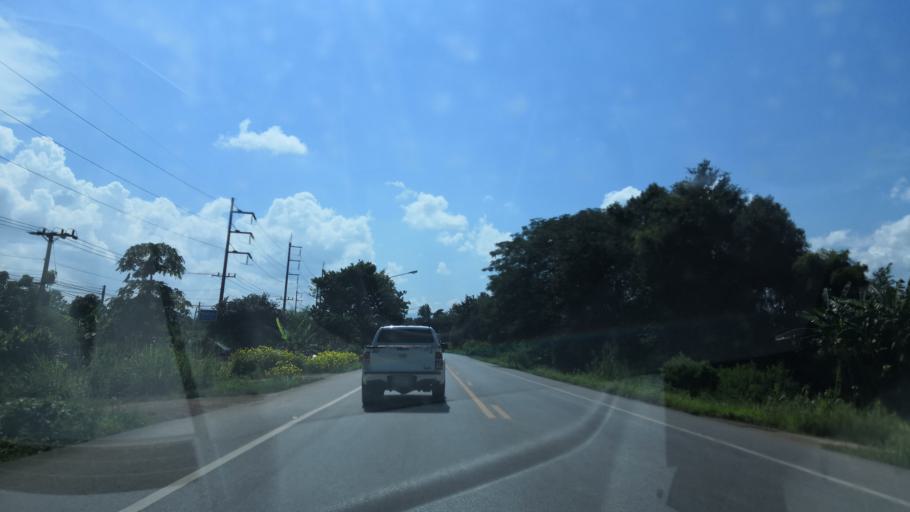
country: TH
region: Chiang Rai
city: Mae Suai
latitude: 19.6177
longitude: 99.5116
